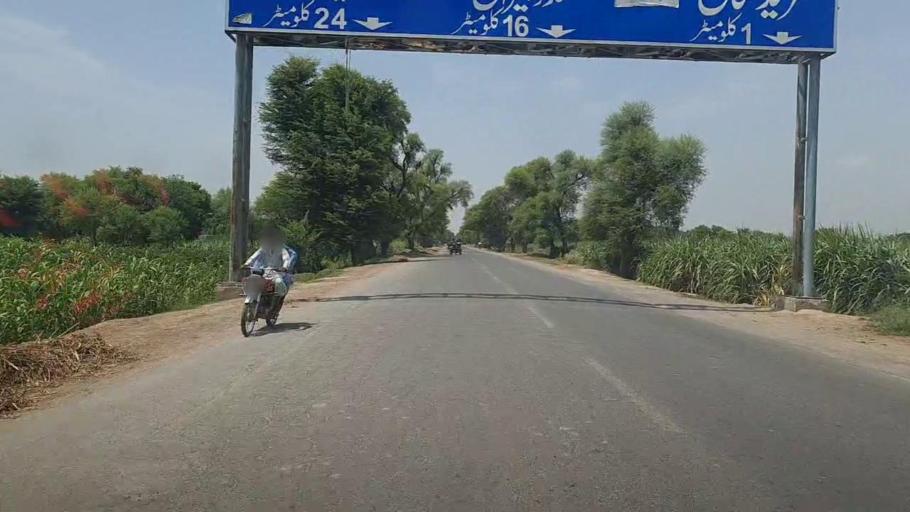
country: PK
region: Sindh
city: Ubauro
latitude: 28.3178
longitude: 69.8063
